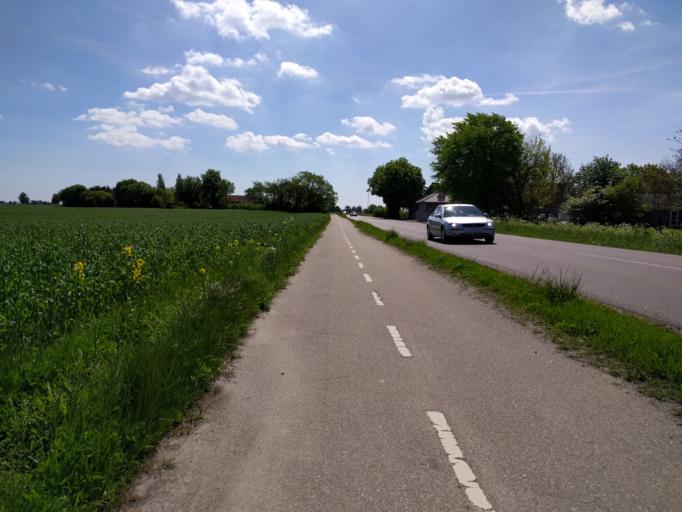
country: DK
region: Zealand
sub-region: Guldborgsund Kommune
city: Nykobing Falster
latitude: 54.7509
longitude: 11.9350
